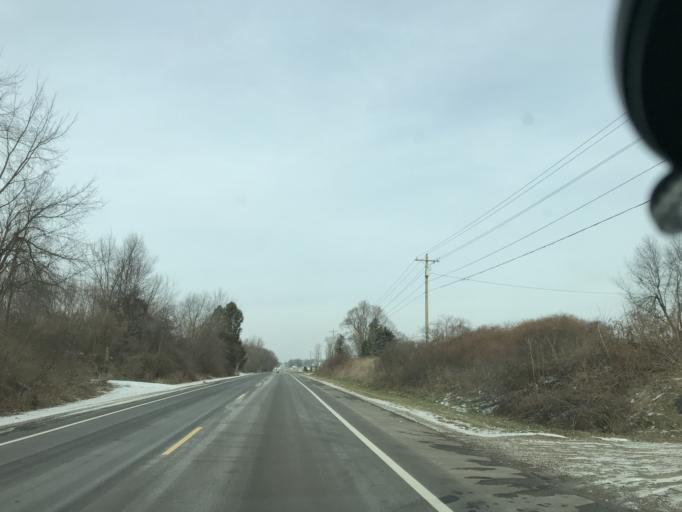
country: US
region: Michigan
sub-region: Ionia County
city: Lake Odessa
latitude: 42.7910
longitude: -85.0744
